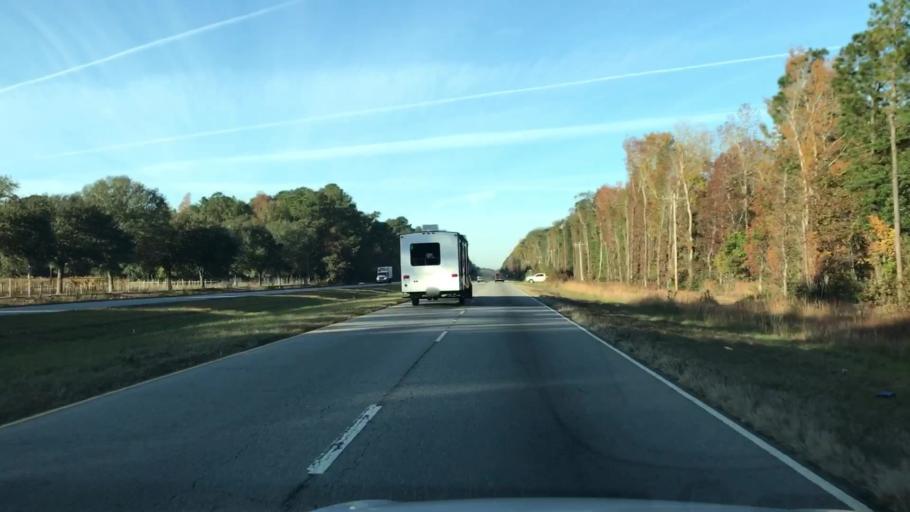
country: US
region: South Carolina
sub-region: Charleston County
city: Ravenel
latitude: 32.7736
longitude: -80.2627
